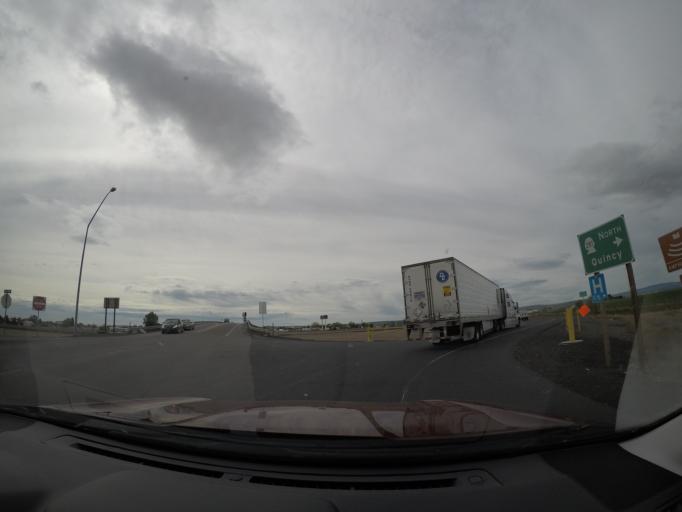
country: US
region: Washington
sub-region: Grant County
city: Quincy
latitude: 47.0864
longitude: -119.8627
